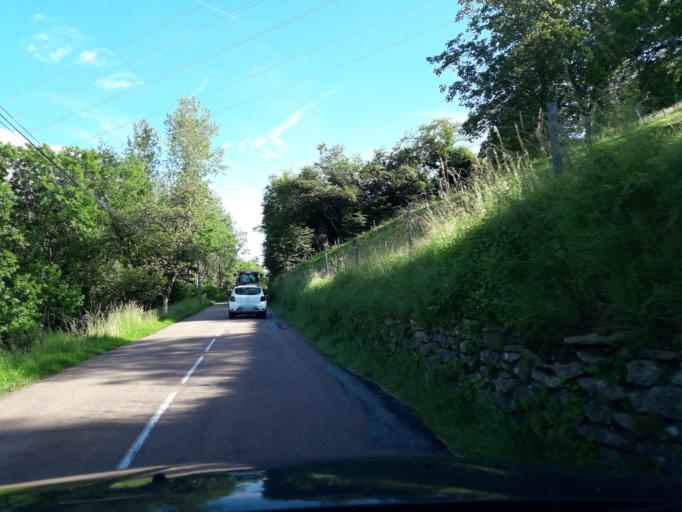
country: FR
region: Rhone-Alpes
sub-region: Departement de la Savoie
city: La Bridoire
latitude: 45.5383
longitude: 5.7612
